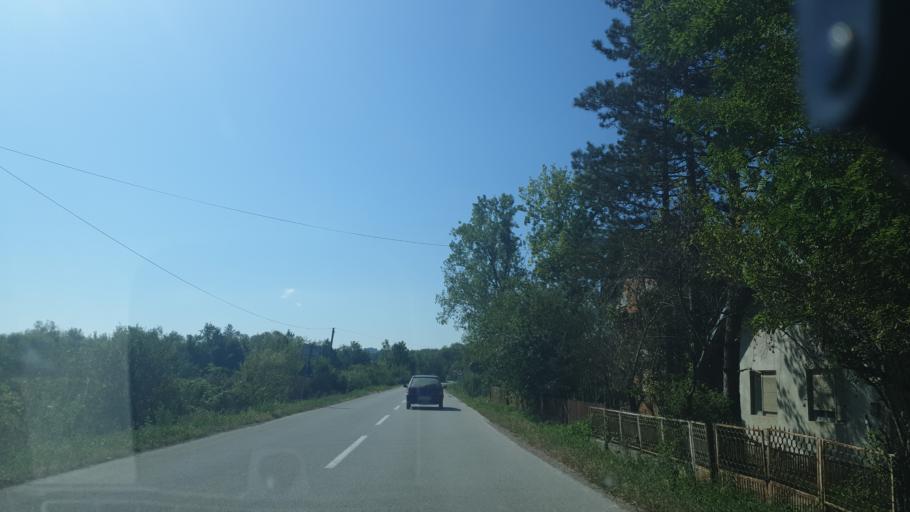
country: RS
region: Central Serbia
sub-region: Kolubarski Okrug
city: Mionica
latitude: 44.2847
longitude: 20.1111
